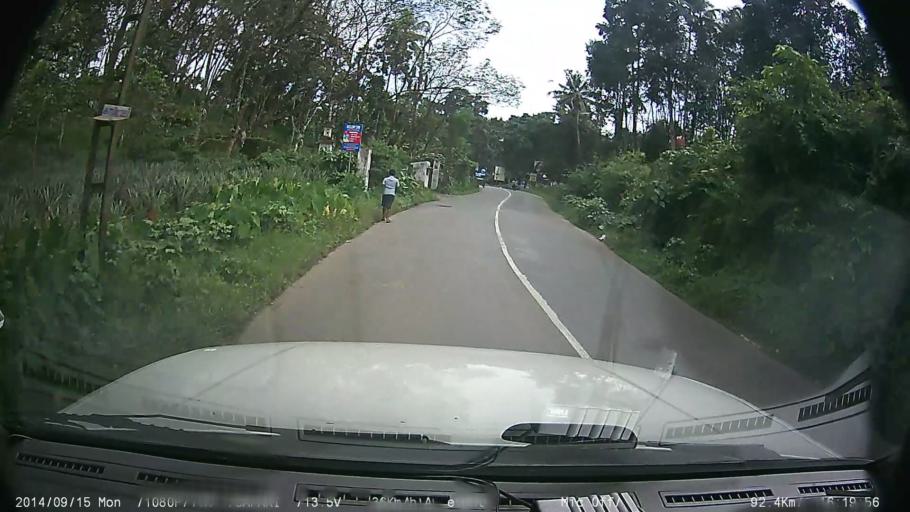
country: IN
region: Kerala
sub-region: Ernakulam
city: Muvattupuzha
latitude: 9.9052
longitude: 76.5858
